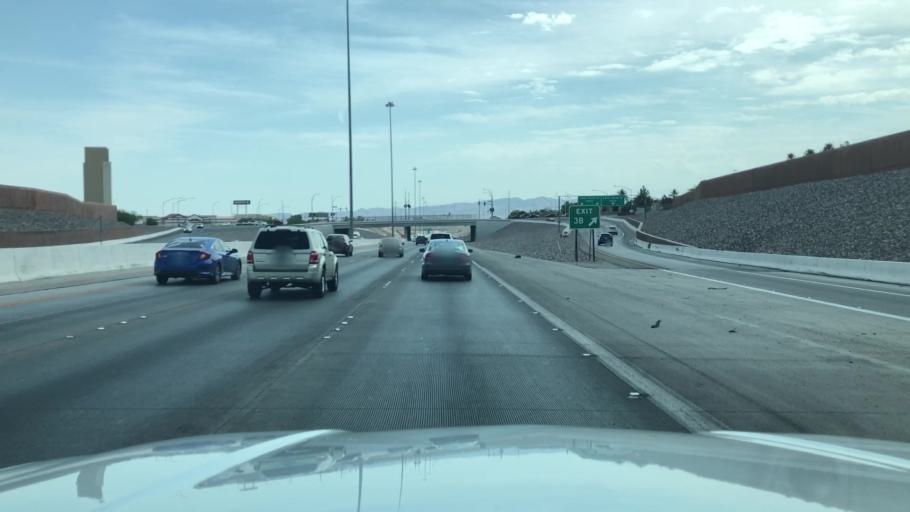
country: US
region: Nevada
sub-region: Clark County
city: Whitney
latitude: 36.0269
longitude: -115.0662
